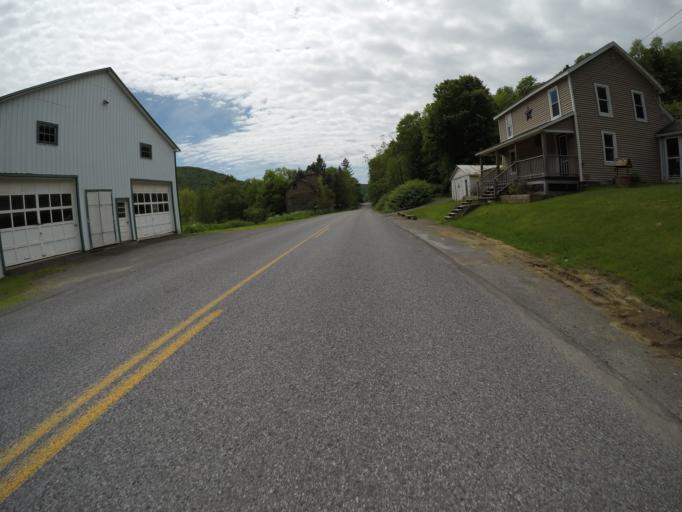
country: US
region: New York
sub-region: Delaware County
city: Stamford
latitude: 42.2001
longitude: -74.5771
